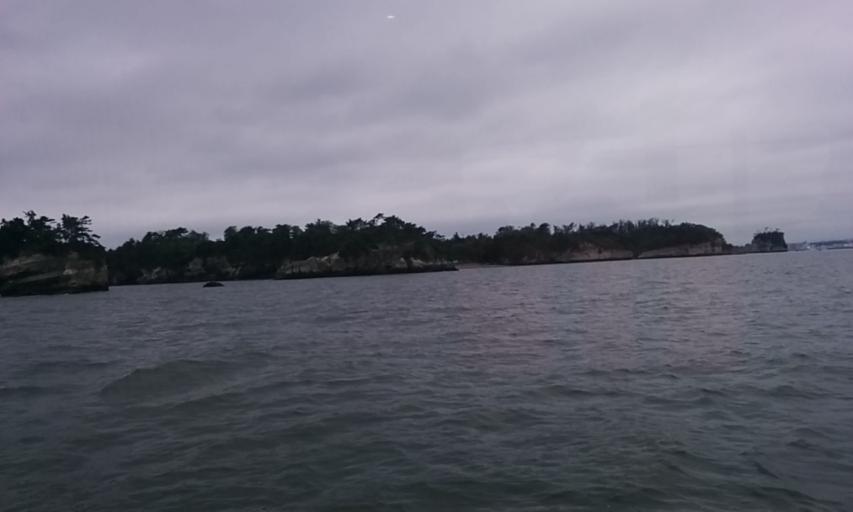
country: JP
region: Miyagi
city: Shiogama
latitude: 38.3297
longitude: 141.0767
